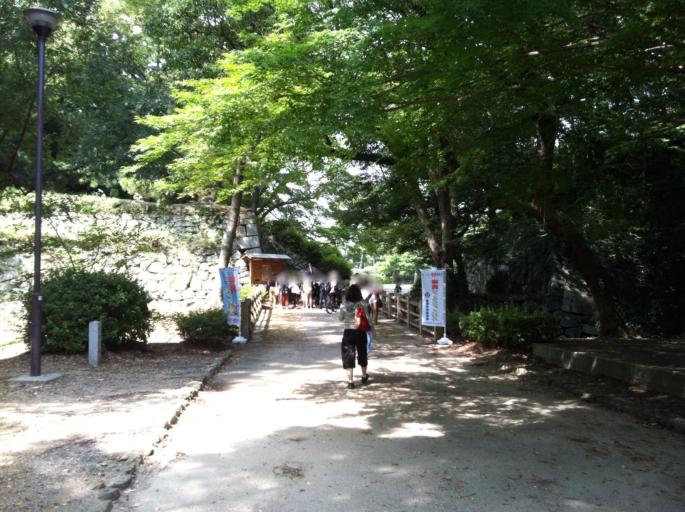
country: JP
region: Aichi
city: Toyohashi
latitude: 34.7696
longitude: 137.3930
